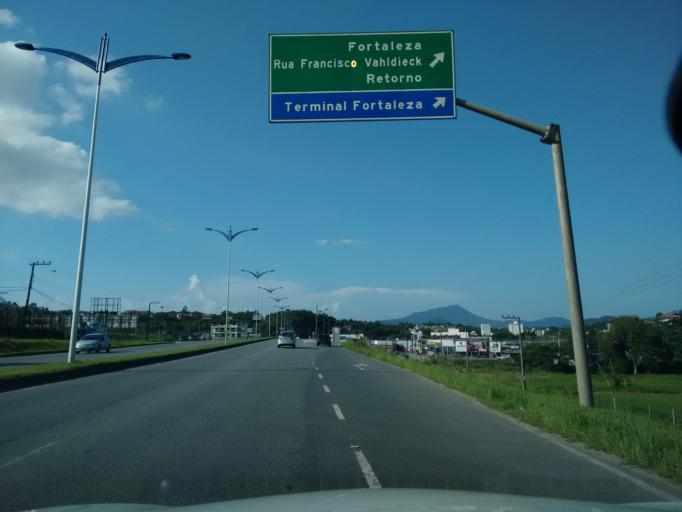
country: BR
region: Santa Catarina
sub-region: Blumenau
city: Blumenau
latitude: -26.8844
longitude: -49.0695
